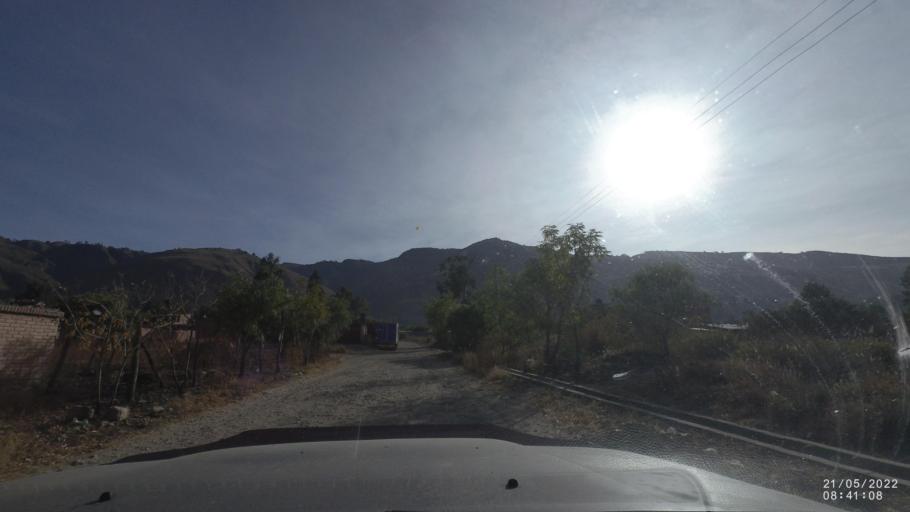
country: BO
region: Cochabamba
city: Cochabamba
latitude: -17.3837
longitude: -66.0420
